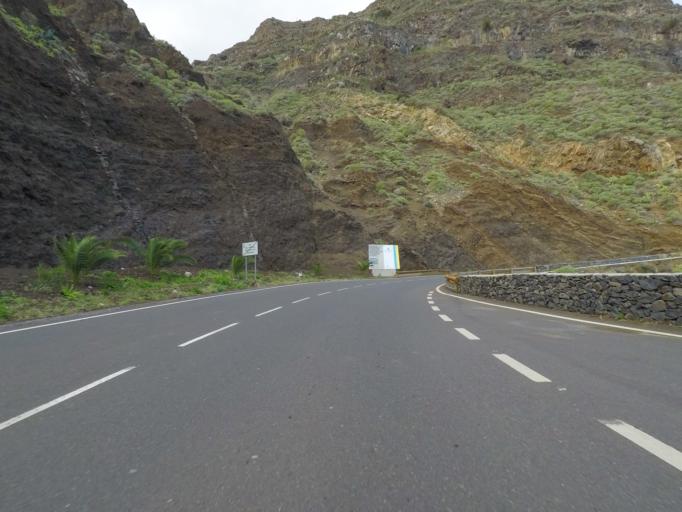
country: ES
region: Canary Islands
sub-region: Provincia de Santa Cruz de Tenerife
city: Agulo
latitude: 28.1811
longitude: -17.1871
